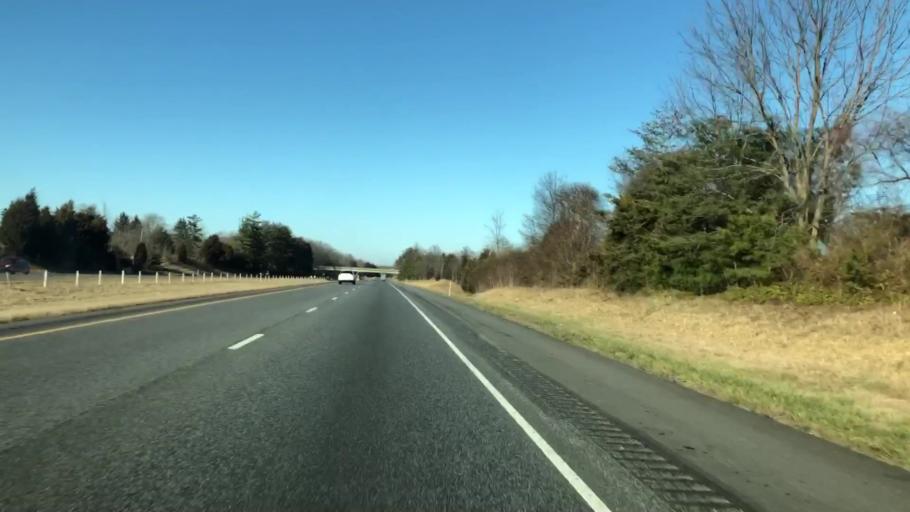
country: US
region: Indiana
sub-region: Scott County
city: Scottsburg
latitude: 38.6442
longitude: -85.7834
